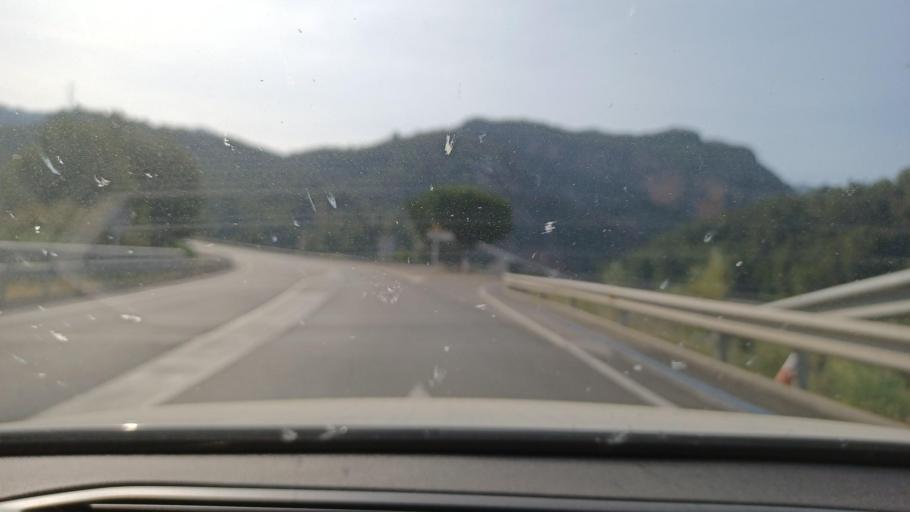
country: ES
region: Catalonia
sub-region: Provincia de Tarragona
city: Benifallet
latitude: 40.9798
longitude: 0.5260
